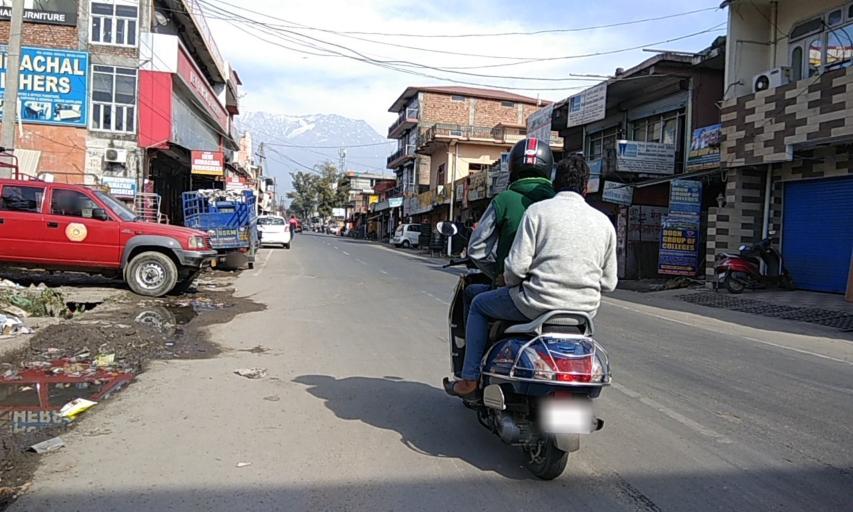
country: IN
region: Himachal Pradesh
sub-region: Kangra
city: Kangra
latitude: 32.1122
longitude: 76.2797
